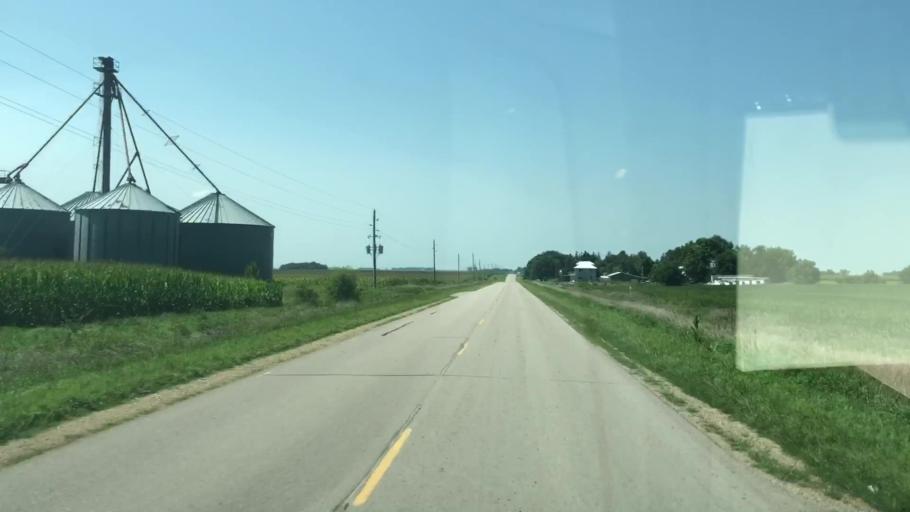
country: US
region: Iowa
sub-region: O'Brien County
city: Sheldon
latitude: 43.2443
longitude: -95.7772
